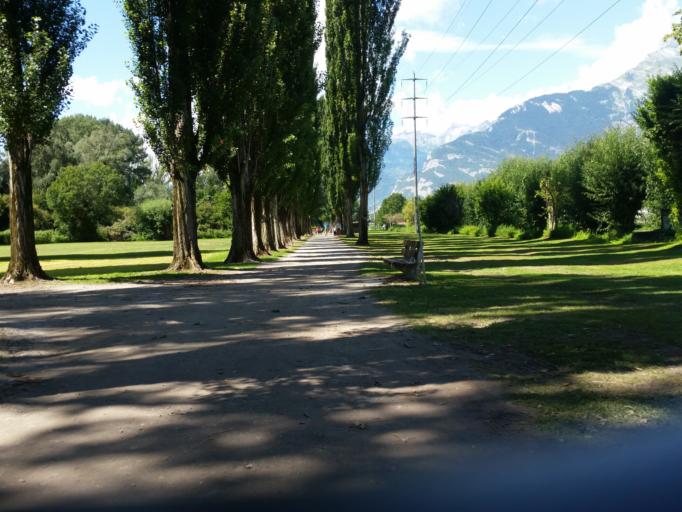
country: CH
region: Valais
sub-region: Conthey District
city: Conthey
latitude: 46.2136
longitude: 7.3264
